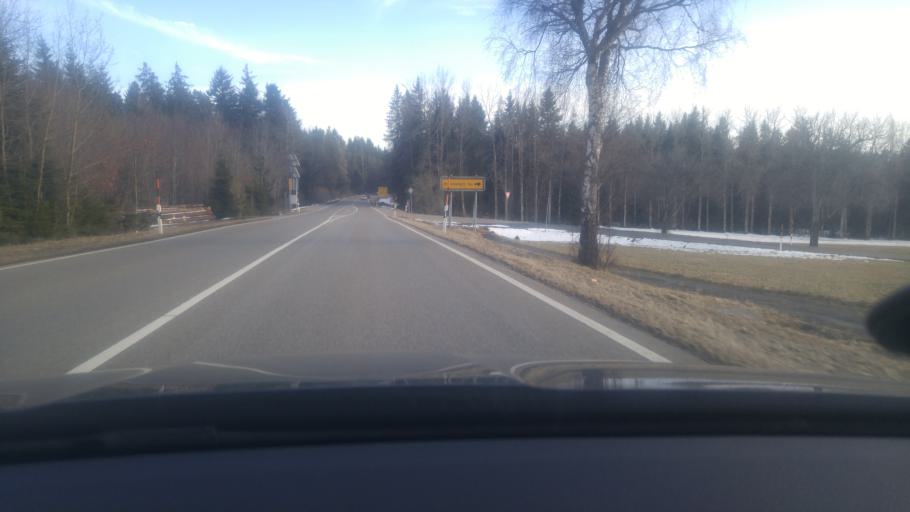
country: DE
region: Baden-Wuerttemberg
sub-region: Freiburg Region
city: Hochenschwand
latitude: 47.6900
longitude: 8.1545
